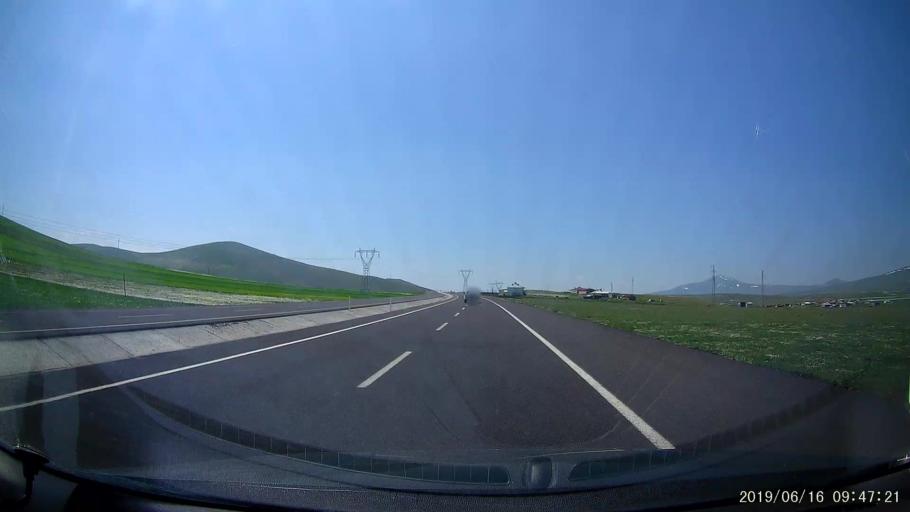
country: TR
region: Kars
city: Digor
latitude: 40.4491
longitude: 43.3429
